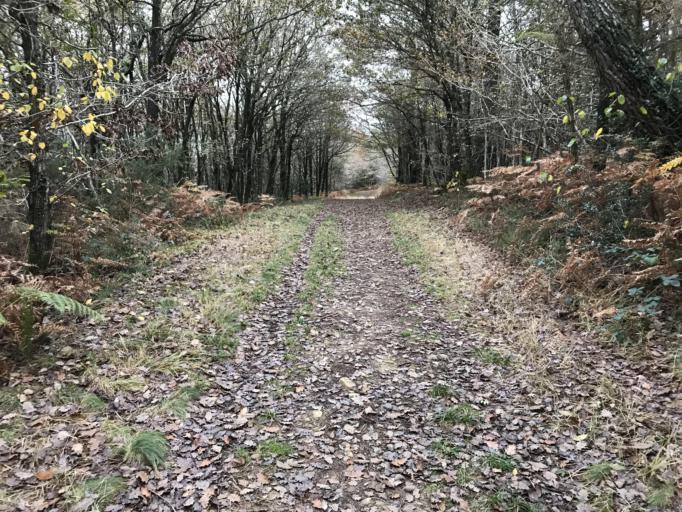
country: FR
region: Brittany
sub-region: Departement du Finistere
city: Hopital-Camfrout
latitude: 48.3344
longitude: -4.2172
